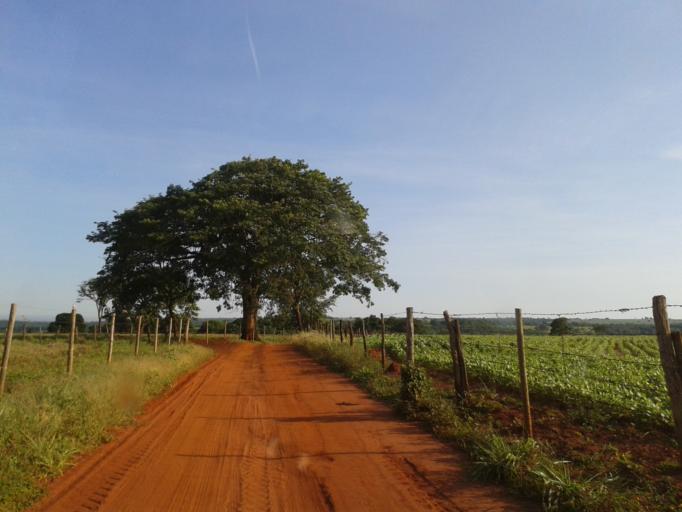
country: BR
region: Minas Gerais
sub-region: Centralina
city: Centralina
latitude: -18.7163
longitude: -49.1972
